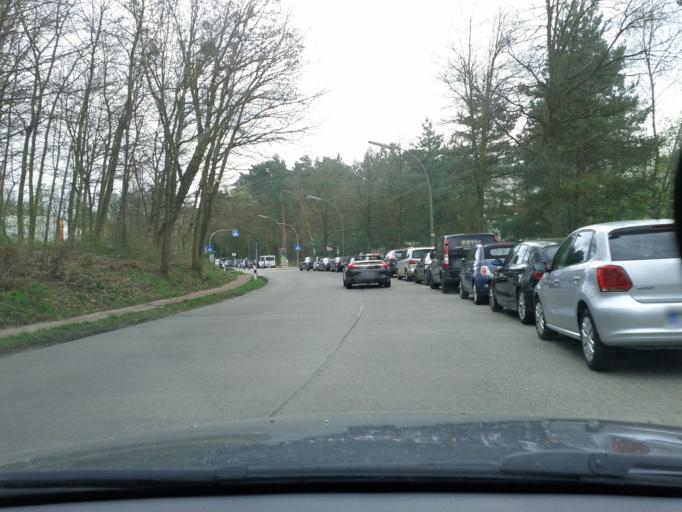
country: DE
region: Berlin
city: Dahlem
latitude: 52.4583
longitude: 13.2624
